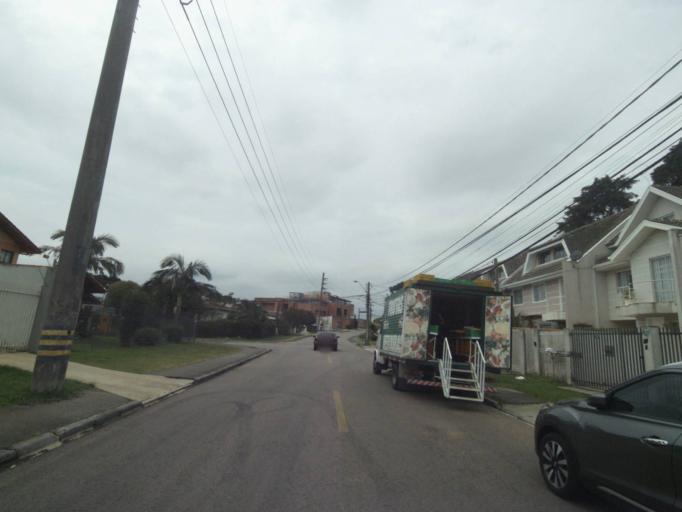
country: BR
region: Parana
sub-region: Curitiba
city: Curitiba
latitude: -25.4108
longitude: -49.2933
